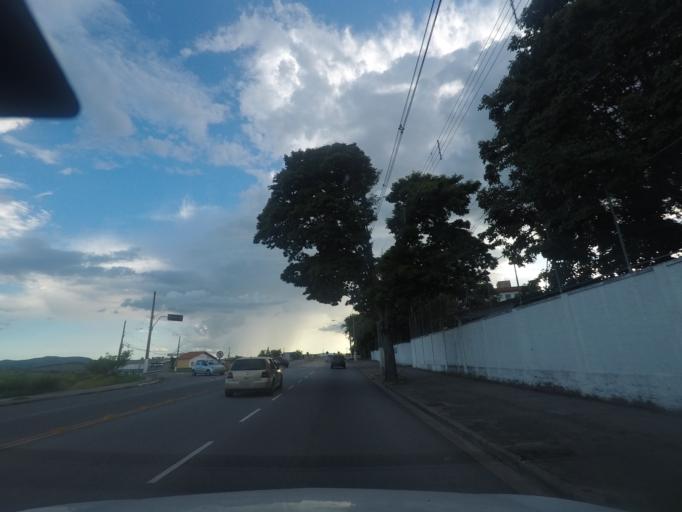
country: BR
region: Sao Paulo
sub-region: Cacapava
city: Cacapava
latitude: -23.1166
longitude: -45.7093
